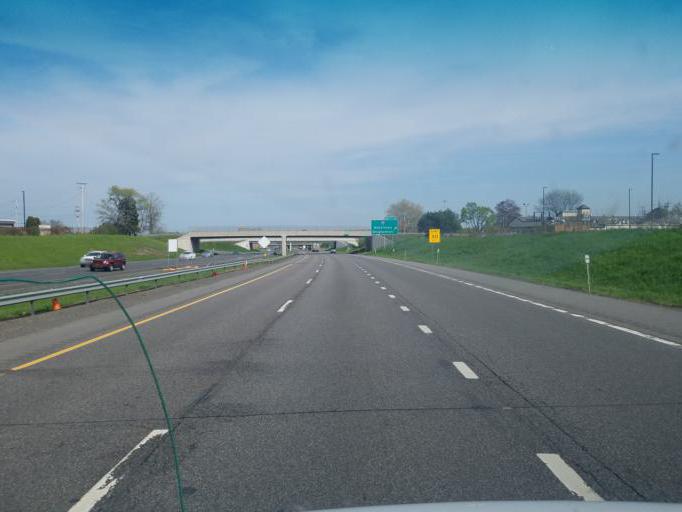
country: US
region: New York
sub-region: Onondaga County
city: Galeville
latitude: 43.0960
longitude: -76.1716
